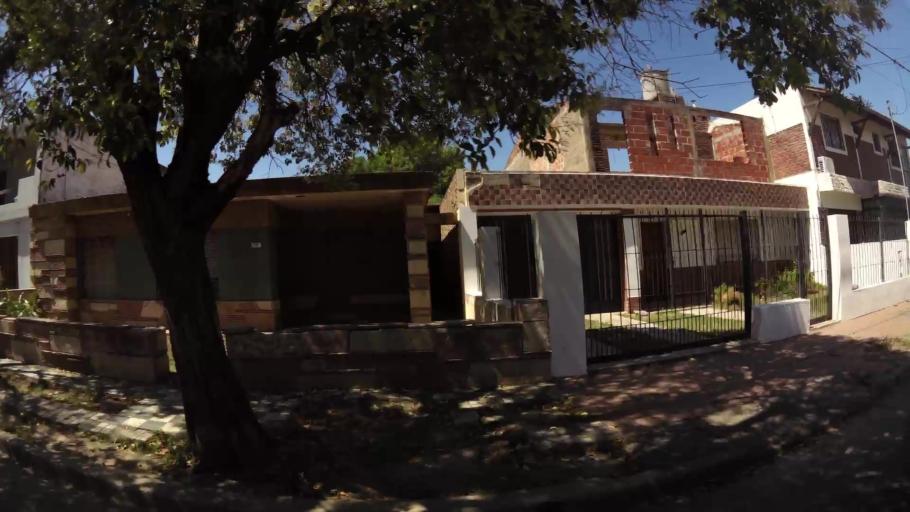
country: AR
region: Cordoba
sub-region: Departamento de Capital
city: Cordoba
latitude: -31.3803
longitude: -64.1578
